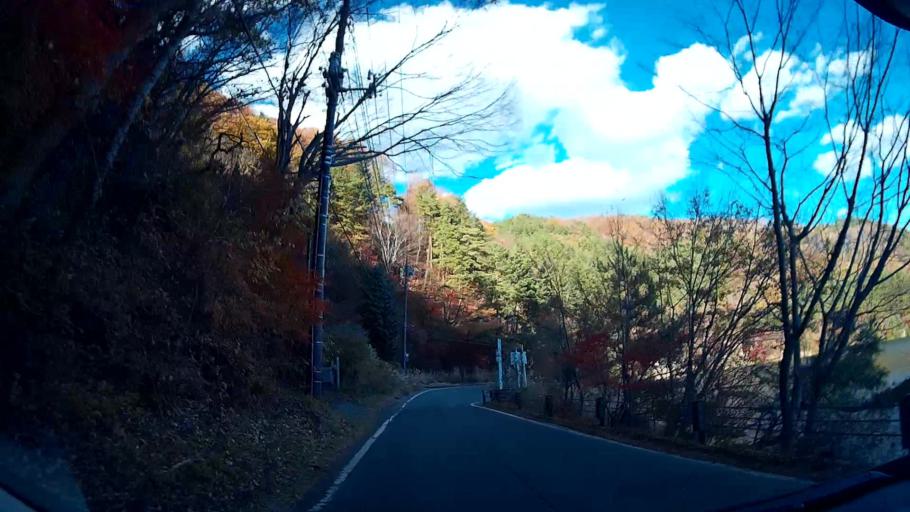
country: JP
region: Yamanashi
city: Fujikawaguchiko
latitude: 35.5138
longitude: 138.7349
